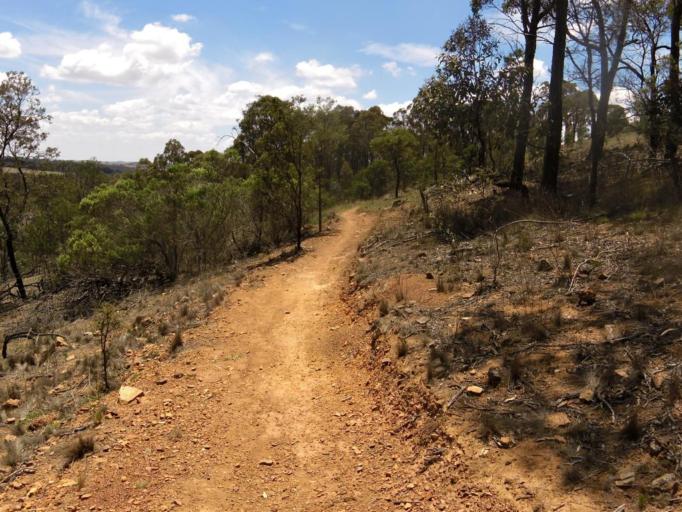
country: AU
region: Australian Capital Territory
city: Kaleen
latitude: -35.1394
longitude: 149.1482
